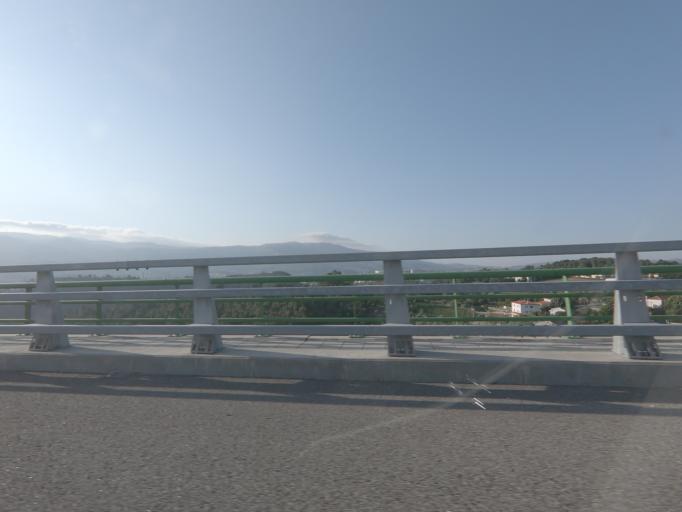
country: PT
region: Vila Real
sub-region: Vila Real
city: Vila Real
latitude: 41.2782
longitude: -7.7478
